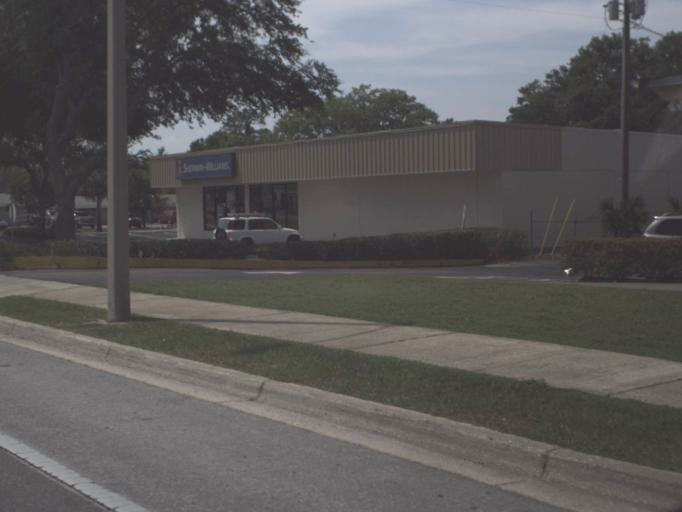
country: US
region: Florida
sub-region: Lake County
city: Eustis
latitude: 28.8340
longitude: -81.6856
